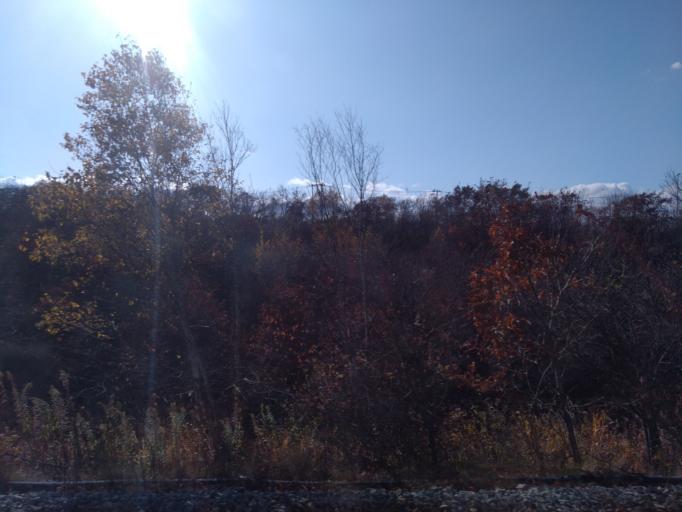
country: JP
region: Hokkaido
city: Chitose
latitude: 42.7859
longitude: 141.7015
